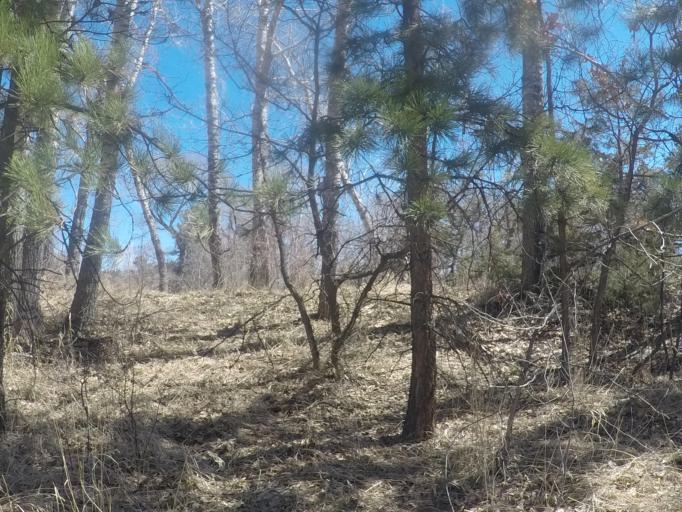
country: US
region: Montana
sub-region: Stillwater County
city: Columbus
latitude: 45.6233
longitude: -109.2895
